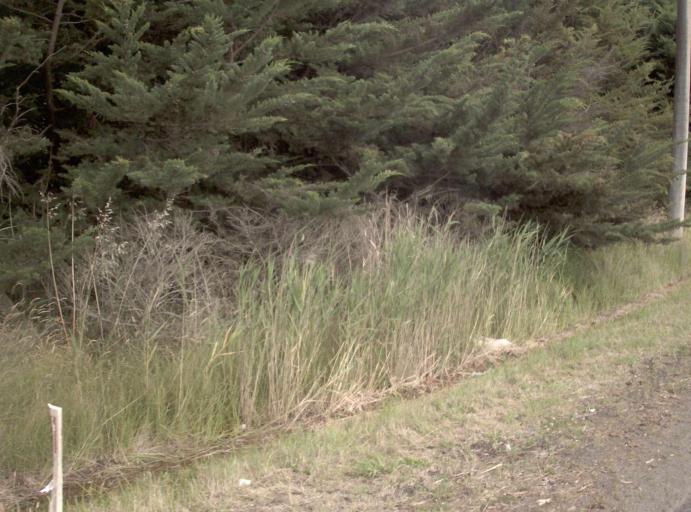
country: AU
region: Victoria
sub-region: Latrobe
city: Morwell
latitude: -38.2162
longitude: 146.4445
